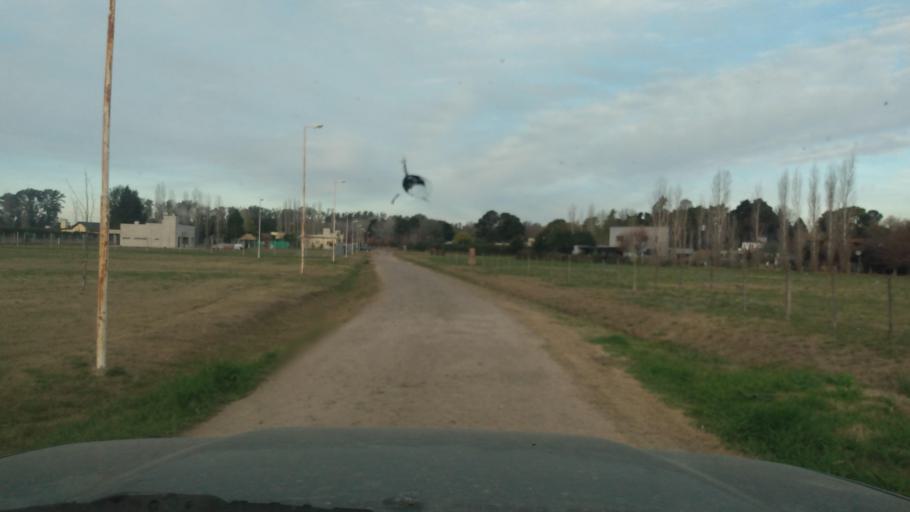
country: AR
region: Buenos Aires
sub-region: Partido de Lujan
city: Lujan
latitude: -34.5751
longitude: -59.0661
